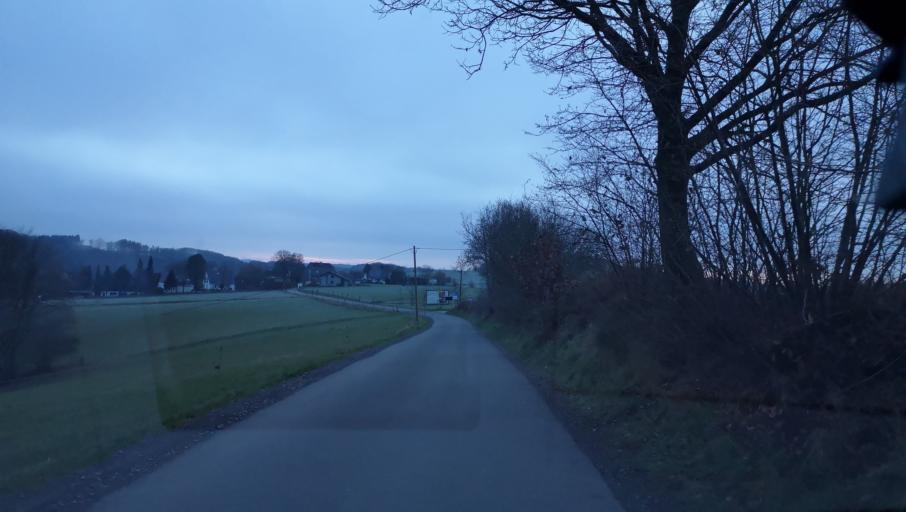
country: DE
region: North Rhine-Westphalia
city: Radevormwald
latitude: 51.1908
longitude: 7.3497
